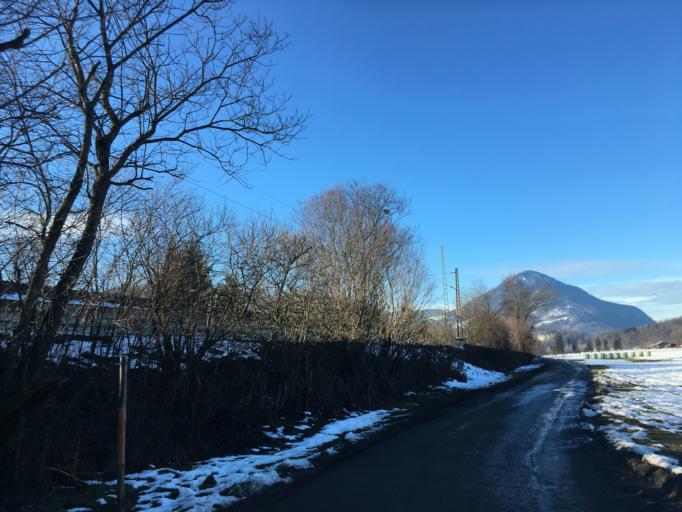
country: DE
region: Bavaria
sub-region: Upper Bavaria
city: Kiefersfelden
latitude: 47.6274
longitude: 12.1933
